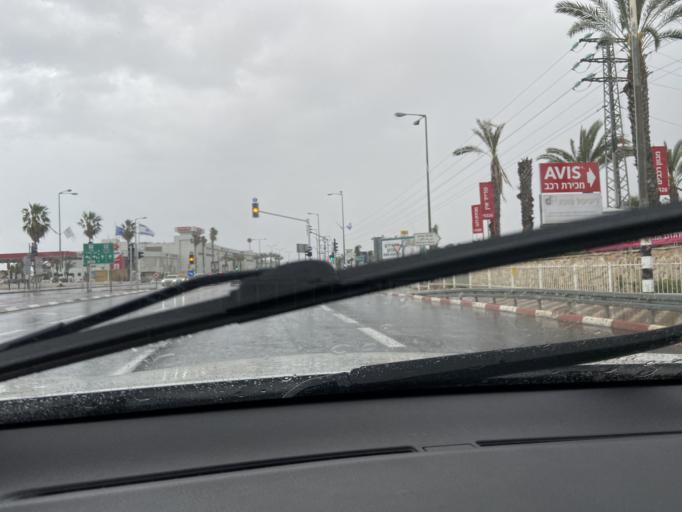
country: IL
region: Northern District
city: El Mazra`a
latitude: 32.9877
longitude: 35.0954
